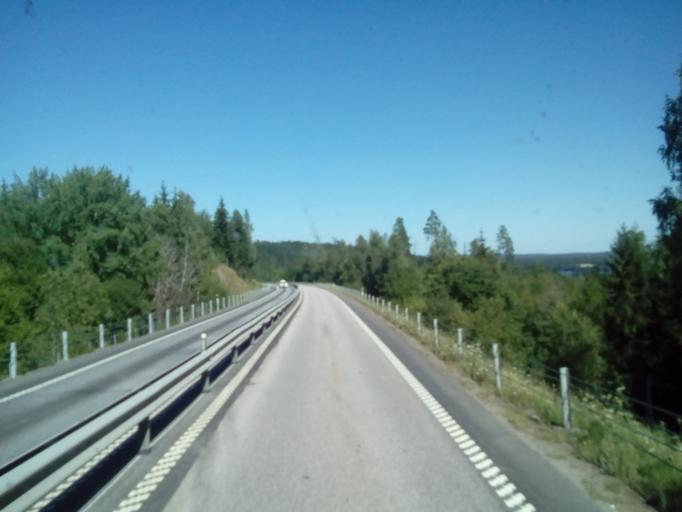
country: SE
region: OEstergoetland
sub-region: Kinda Kommun
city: Rimforsa
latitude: 58.0985
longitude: 15.6661
